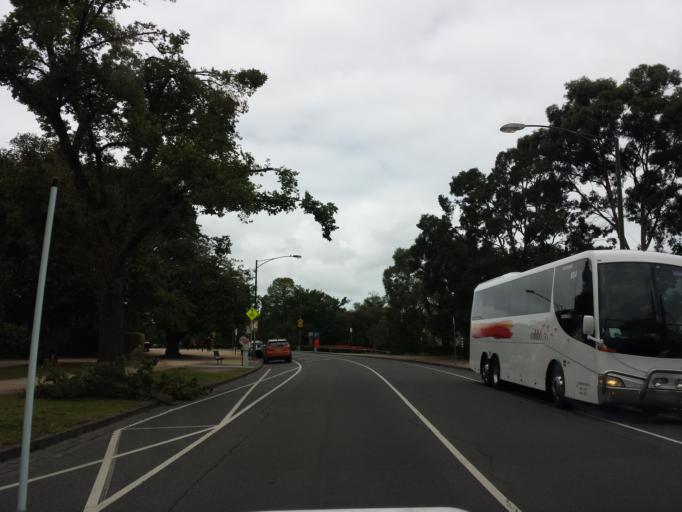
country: AU
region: Victoria
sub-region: Port Phillip
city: South Melbourne
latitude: -37.8294
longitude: 144.9742
